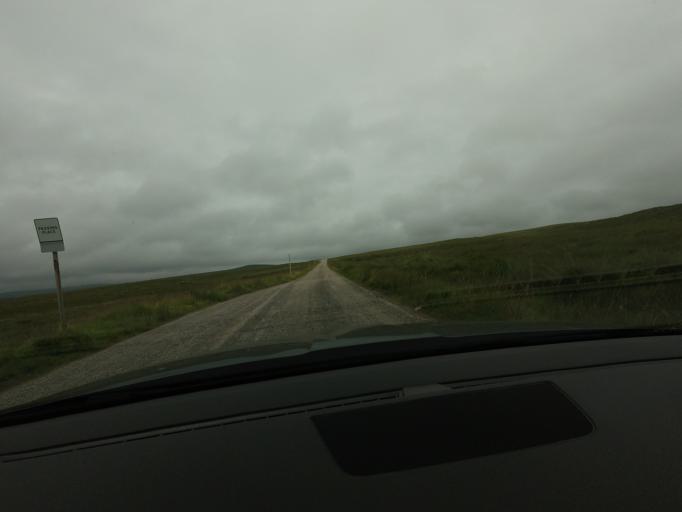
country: GB
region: Scotland
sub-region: Highland
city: Golspie
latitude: 58.3156
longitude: -4.4282
